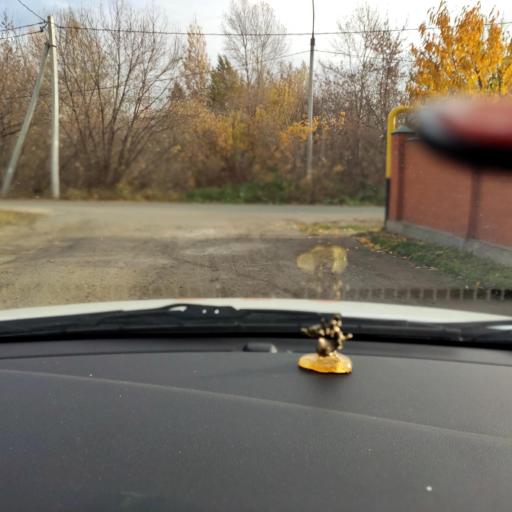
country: RU
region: Tatarstan
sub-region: Gorod Kazan'
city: Kazan
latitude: 55.7368
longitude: 49.0969
